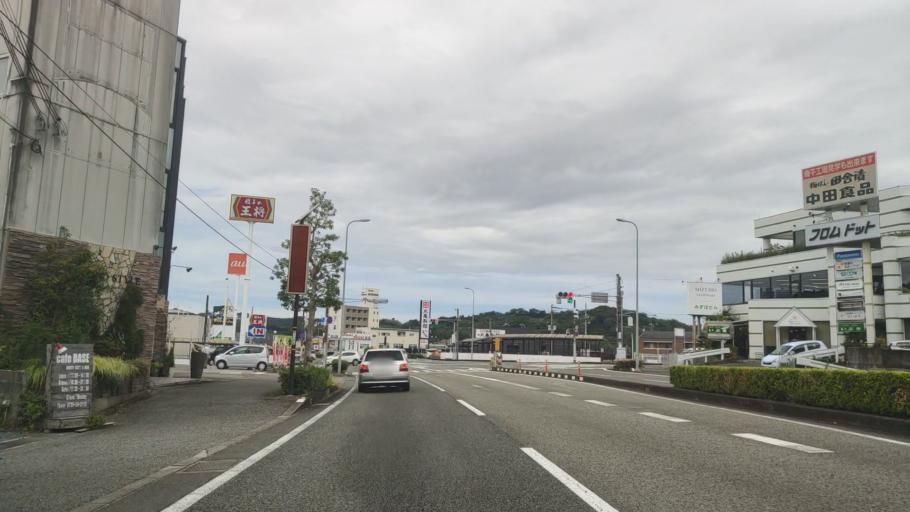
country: JP
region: Wakayama
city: Tanabe
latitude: 33.7398
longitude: 135.3934
